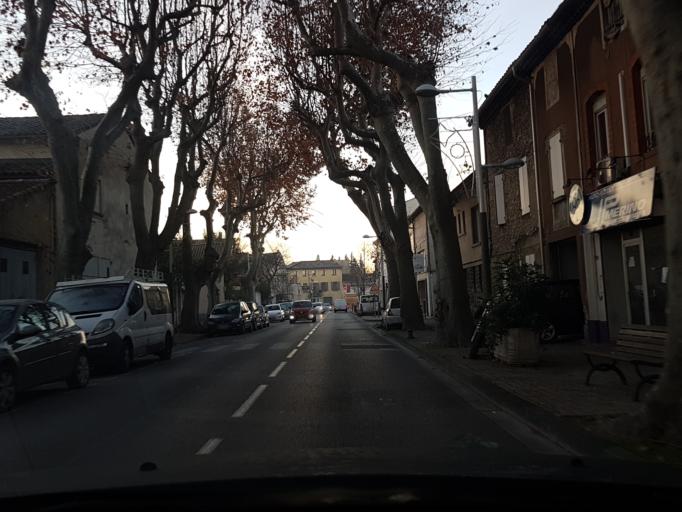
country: FR
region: Provence-Alpes-Cote d'Azur
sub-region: Departement du Vaucluse
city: Monteux
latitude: 44.0360
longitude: 4.9992
